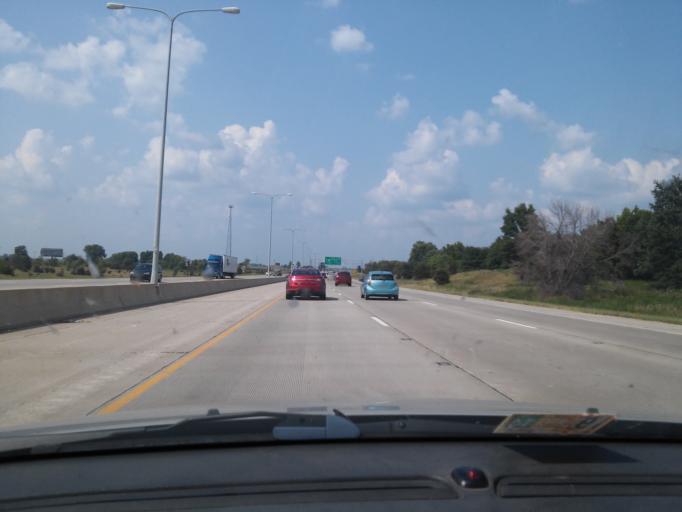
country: US
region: Illinois
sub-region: McLean County
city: Normal
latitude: 40.5114
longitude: -89.0287
